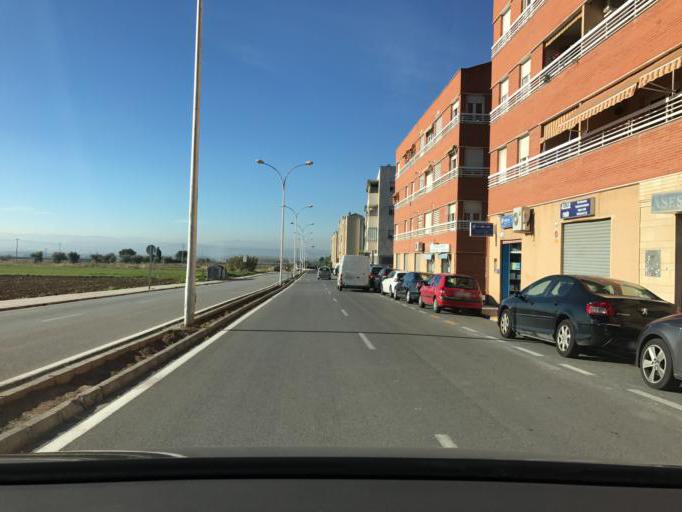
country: ES
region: Andalusia
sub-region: Provincia de Granada
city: Albolote
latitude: 37.2264
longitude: -3.6510
